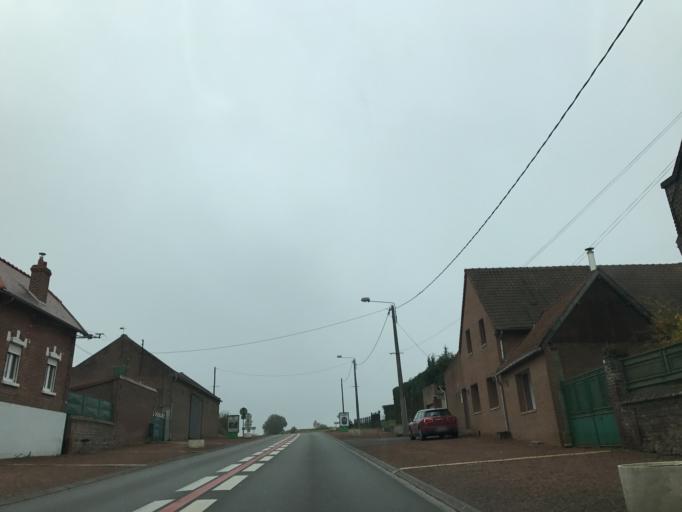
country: FR
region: Nord-Pas-de-Calais
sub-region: Departement du Pas-de-Calais
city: Beaurains
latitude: 50.2118
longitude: 2.8126
